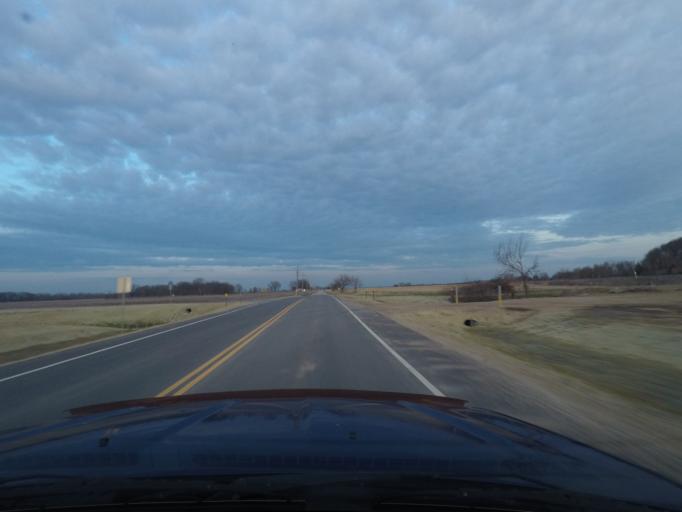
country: US
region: Kansas
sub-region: Douglas County
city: Lawrence
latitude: 38.9569
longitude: -95.2009
